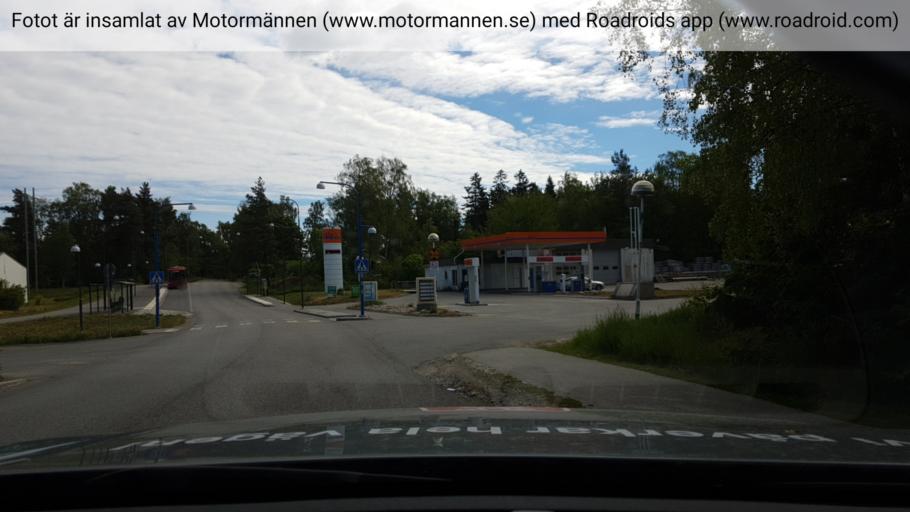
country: SE
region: Stockholm
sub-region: Nynashamns Kommun
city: Osmo
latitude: 58.9821
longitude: 17.8954
